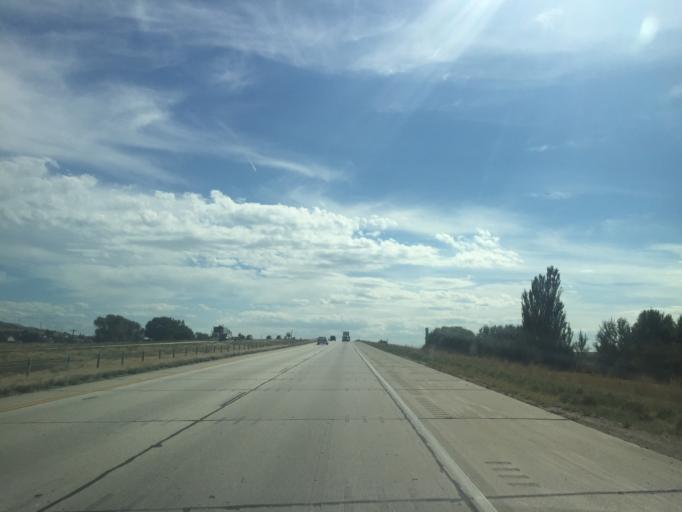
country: US
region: Utah
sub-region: Box Elder County
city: South Willard
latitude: 41.3722
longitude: -112.0428
